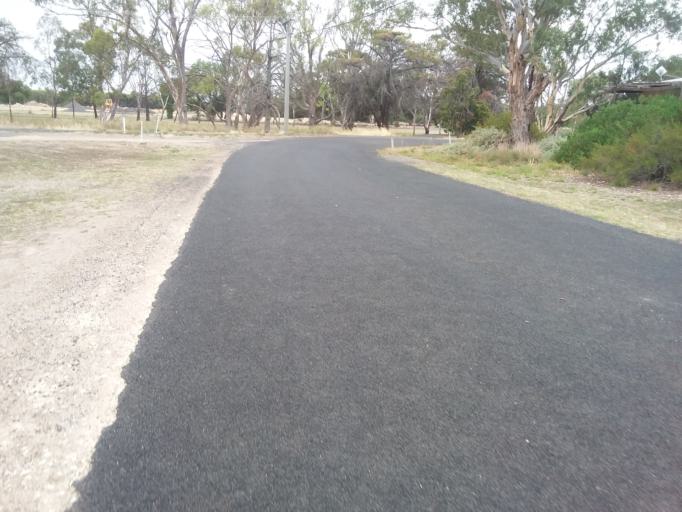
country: AU
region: Victoria
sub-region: Horsham
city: Horsham
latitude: -36.7403
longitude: 141.9390
